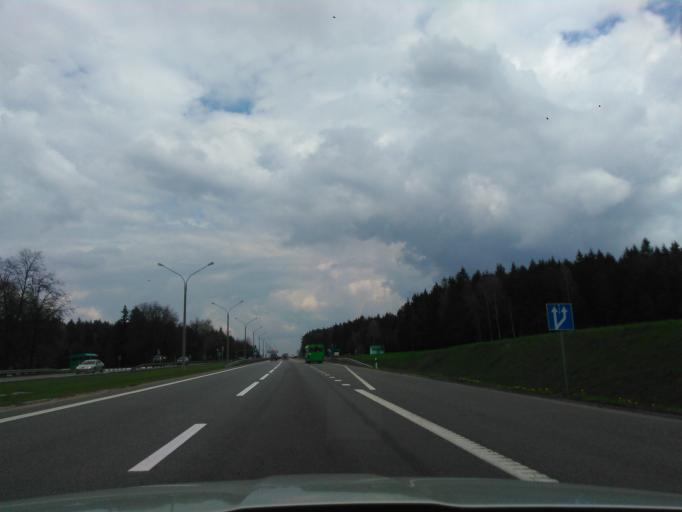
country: BY
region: Minsk
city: Korolev Stan
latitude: 53.9793
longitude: 27.7748
